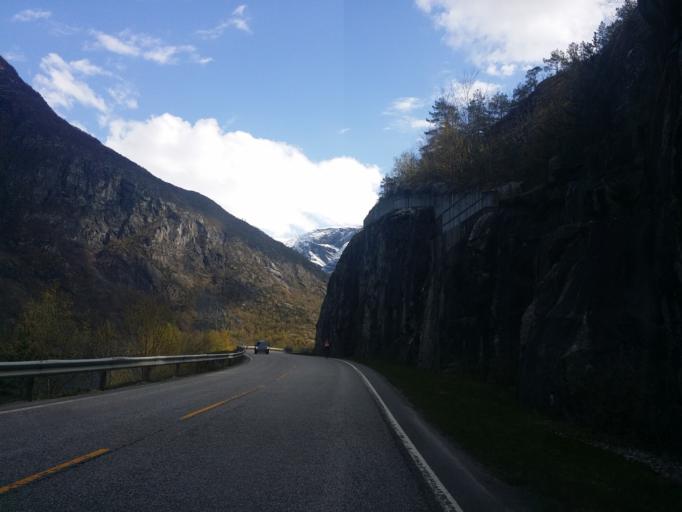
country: NO
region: Hordaland
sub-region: Eidfjord
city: Eidfjord
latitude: 60.4460
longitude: 7.1032
